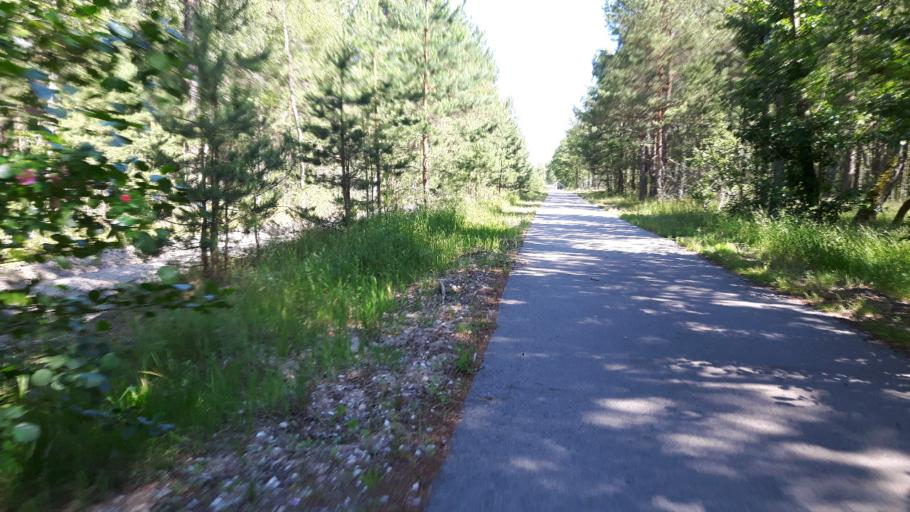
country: LT
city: Neringa
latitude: 55.3411
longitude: 21.0395
